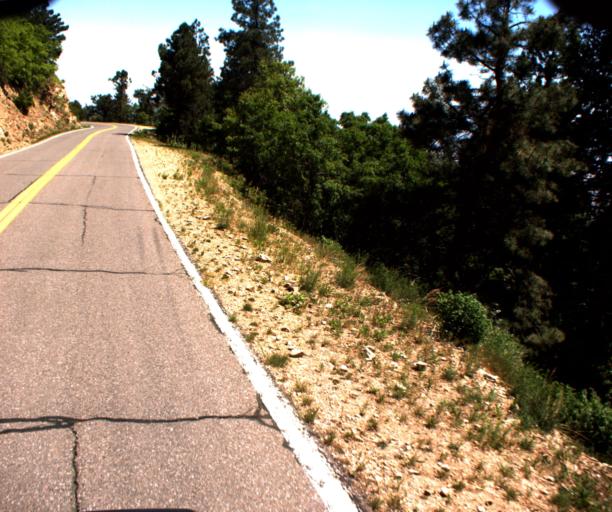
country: US
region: Arizona
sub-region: Graham County
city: Swift Trail Junction
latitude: 32.6448
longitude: -109.8529
